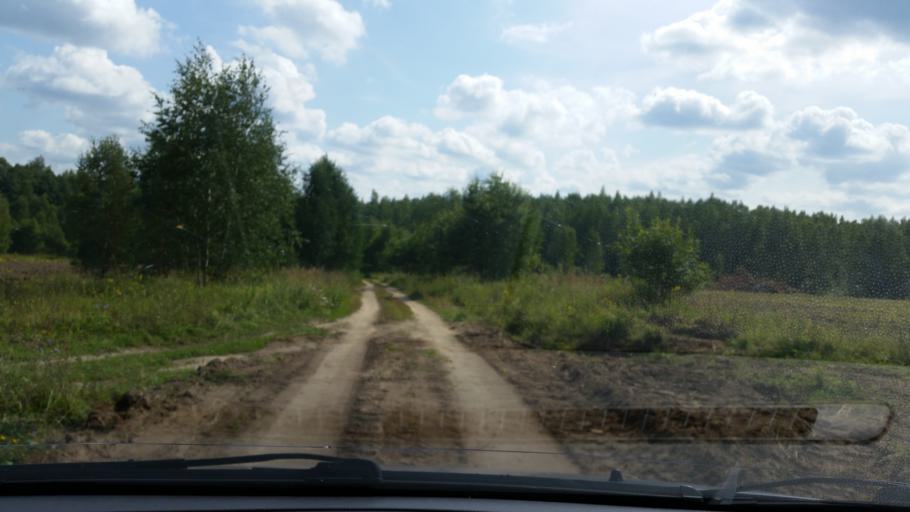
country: RU
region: Moskovskaya
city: Pushchino
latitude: 54.9296
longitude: 37.7049
